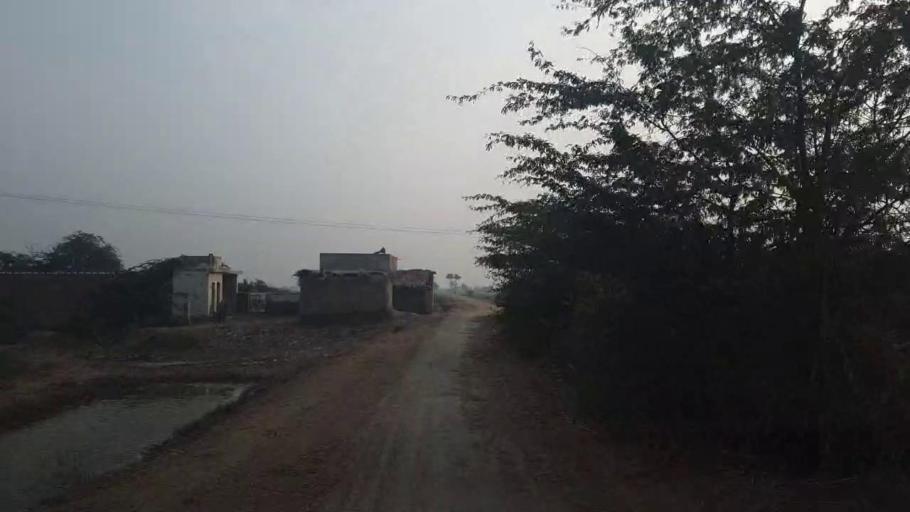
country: PK
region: Sindh
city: Berani
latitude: 25.8031
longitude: 68.7476
